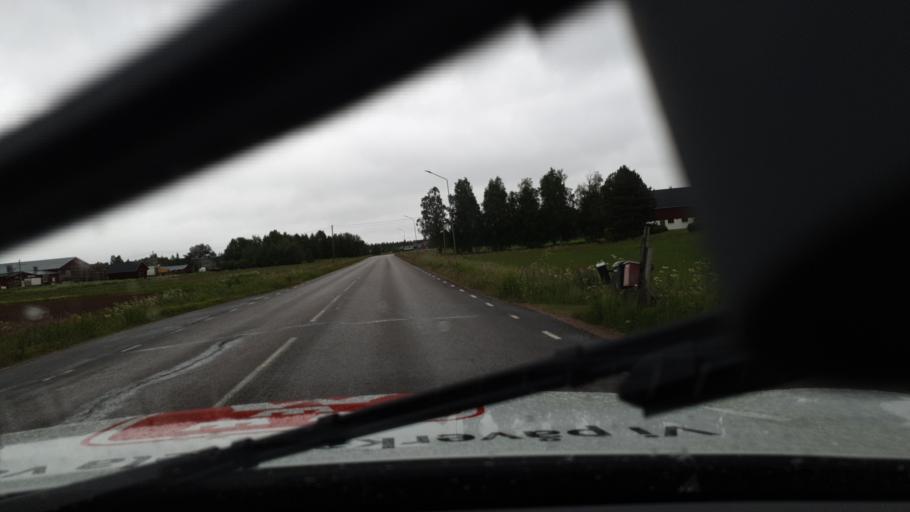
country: SE
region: Norrbotten
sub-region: Overtornea Kommun
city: OEvertornea
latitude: 66.4610
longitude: 23.6348
